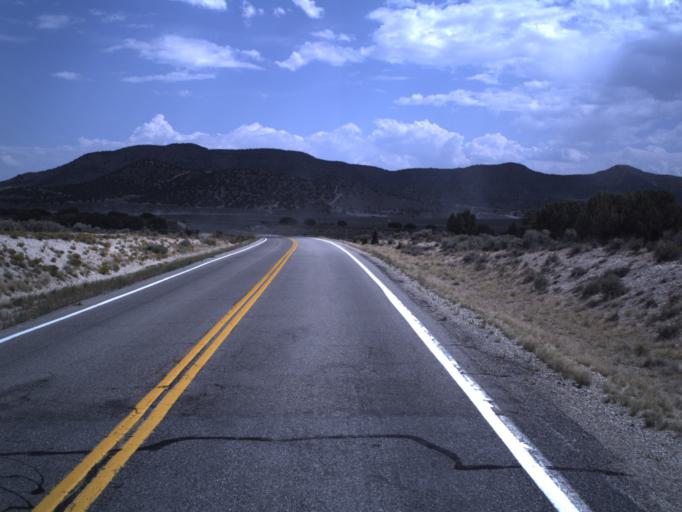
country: US
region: Utah
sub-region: Utah County
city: Eagle Mountain
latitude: 40.2338
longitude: -112.1956
